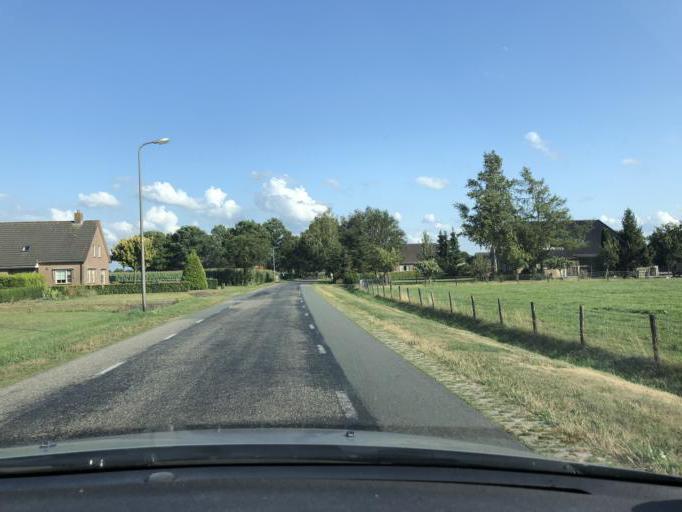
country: NL
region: Overijssel
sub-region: Gemeente Staphorst
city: Staphorst
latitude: 52.6089
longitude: 6.2729
